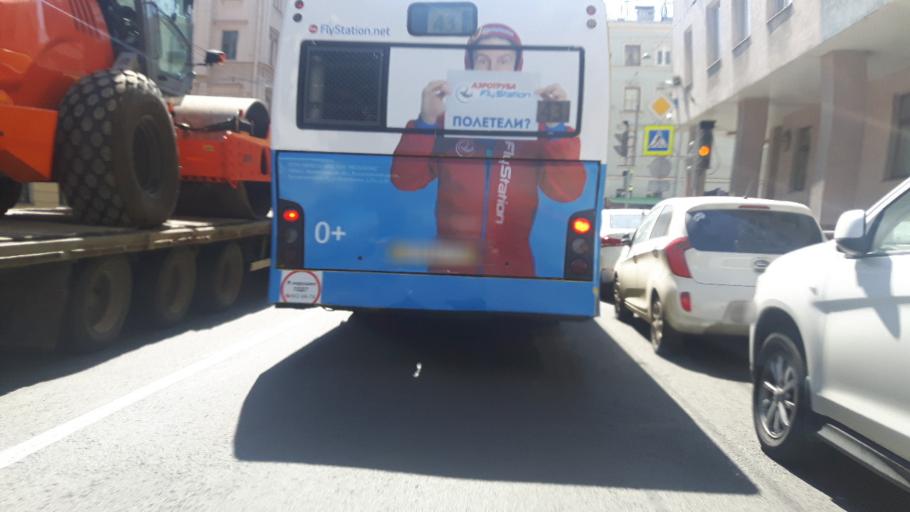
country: RU
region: St.-Petersburg
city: Admiralteisky
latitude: 59.9133
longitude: 30.2975
